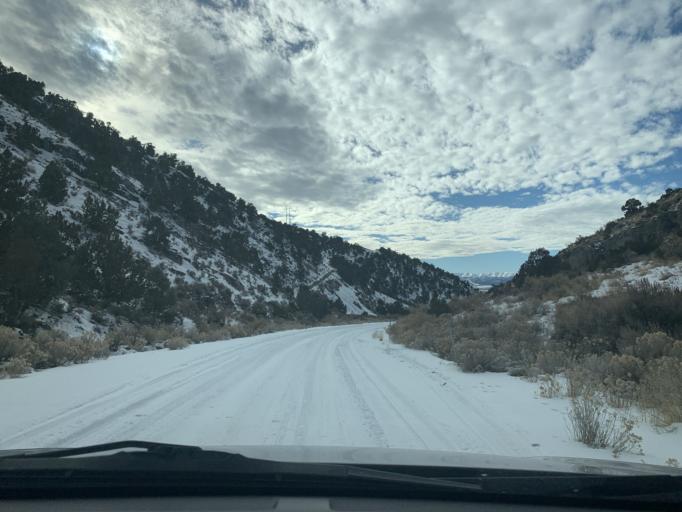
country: US
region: Utah
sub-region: Tooele County
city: Tooele
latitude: 40.3112
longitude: -112.2462
